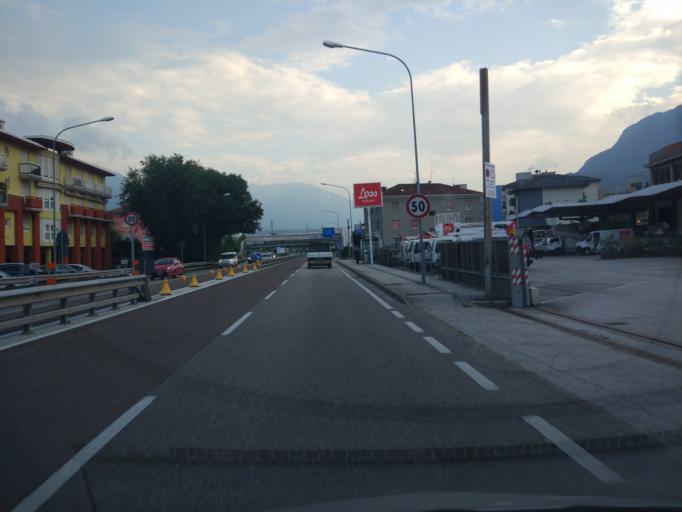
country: IT
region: Trentino-Alto Adige
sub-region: Provincia di Trento
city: Meano
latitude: 46.0995
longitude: 11.1117
